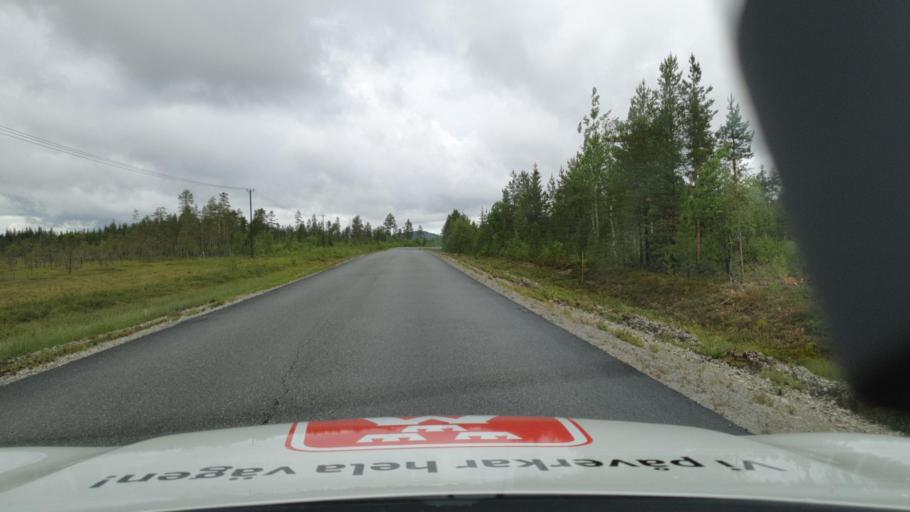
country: SE
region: Vaesterbotten
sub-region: Dorotea Kommun
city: Dorotea
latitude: 64.1288
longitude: 16.6347
